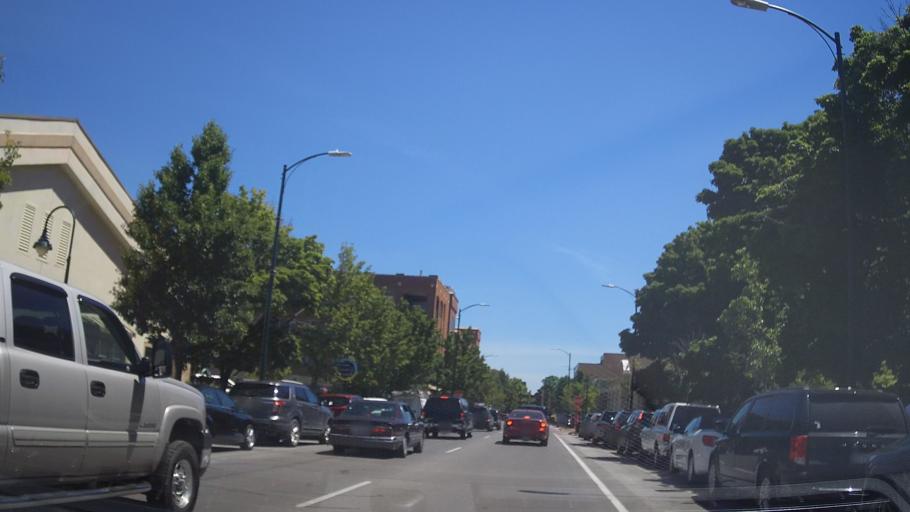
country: US
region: Michigan
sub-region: Grand Traverse County
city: Traverse City
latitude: 44.7629
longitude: -85.6192
